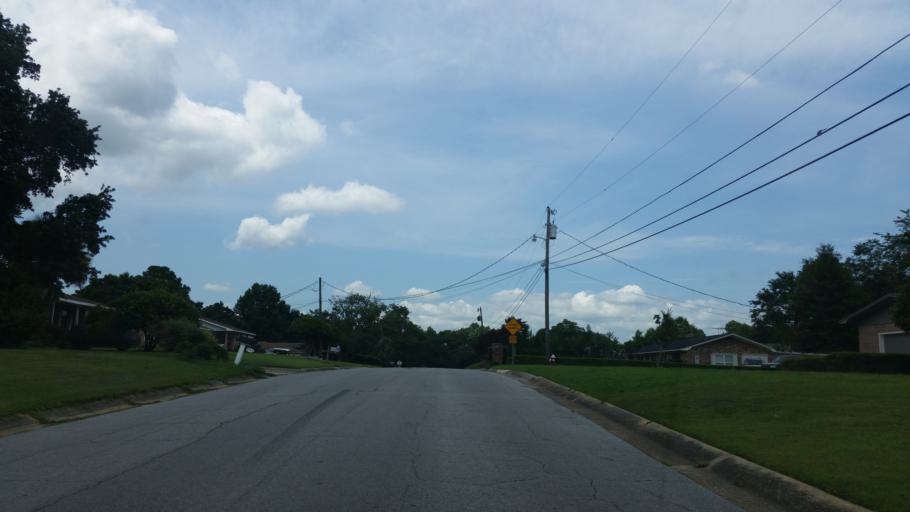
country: US
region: Florida
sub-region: Escambia County
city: Brent
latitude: 30.4924
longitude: -87.2380
